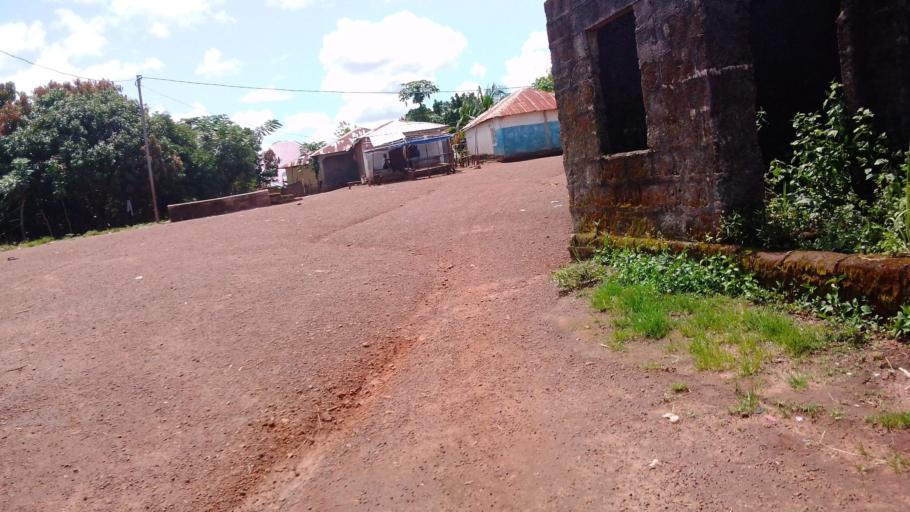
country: SL
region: Northern Province
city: Makeni
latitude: 8.8828
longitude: -12.0289
